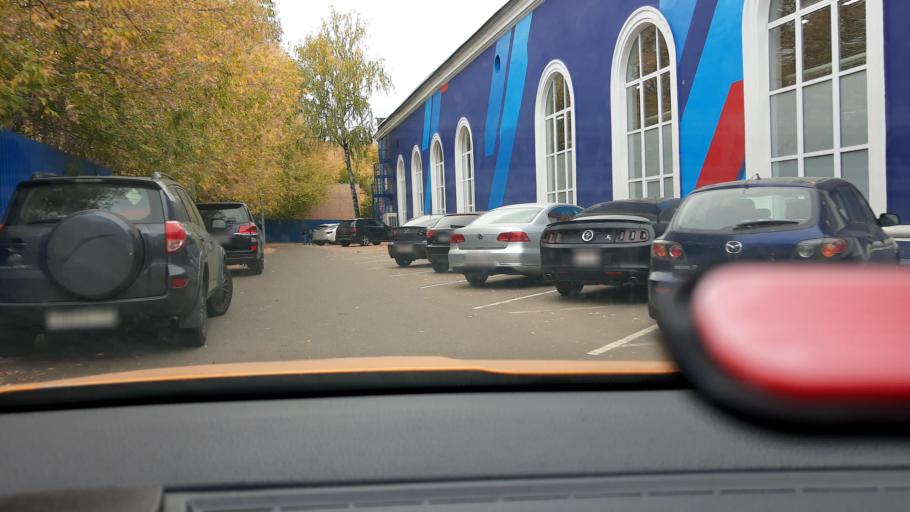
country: RU
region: Moscow
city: Strogino
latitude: 55.8376
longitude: 37.4290
